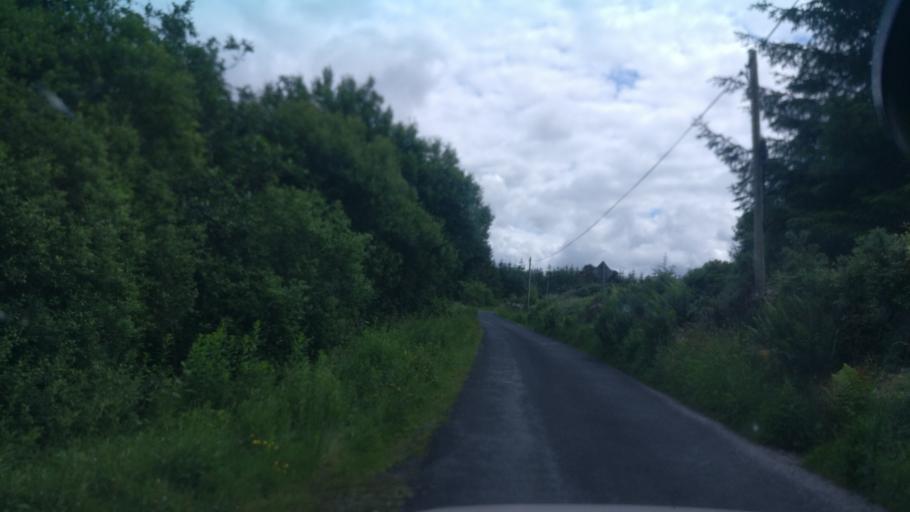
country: IE
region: Connaught
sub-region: County Galway
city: Loughrea
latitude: 53.1473
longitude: -8.5662
